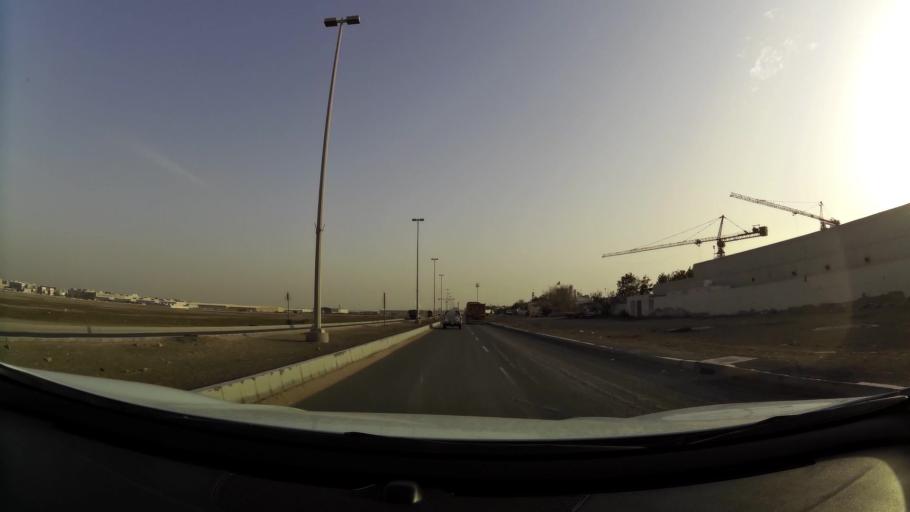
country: AE
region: Abu Dhabi
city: Abu Dhabi
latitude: 24.3437
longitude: 54.5124
